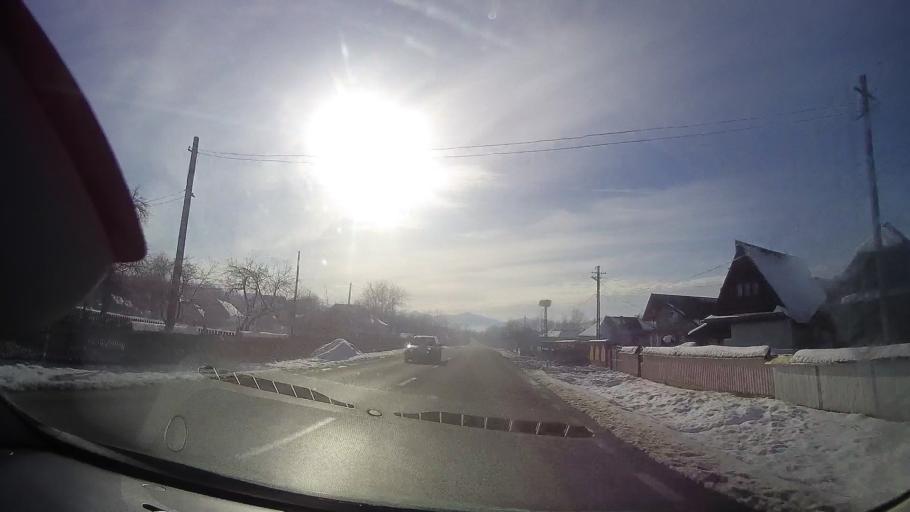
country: RO
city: Vanatori-Neamt
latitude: 47.1683
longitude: 26.3211
